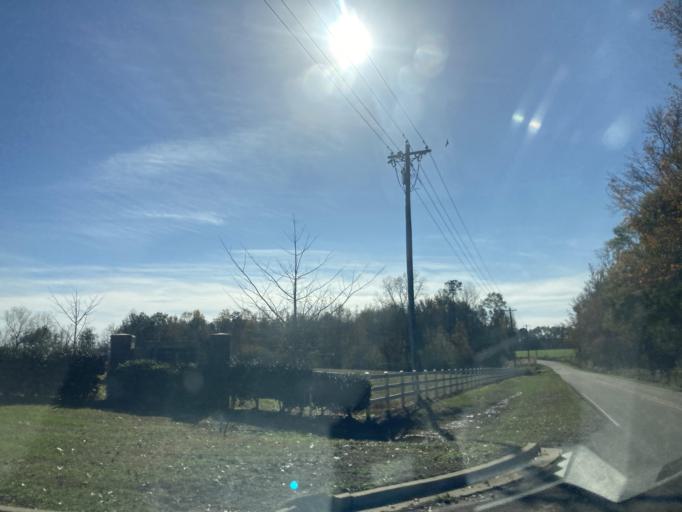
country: US
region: Mississippi
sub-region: Lamar County
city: Sumrall
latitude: 31.2569
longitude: -89.5733
